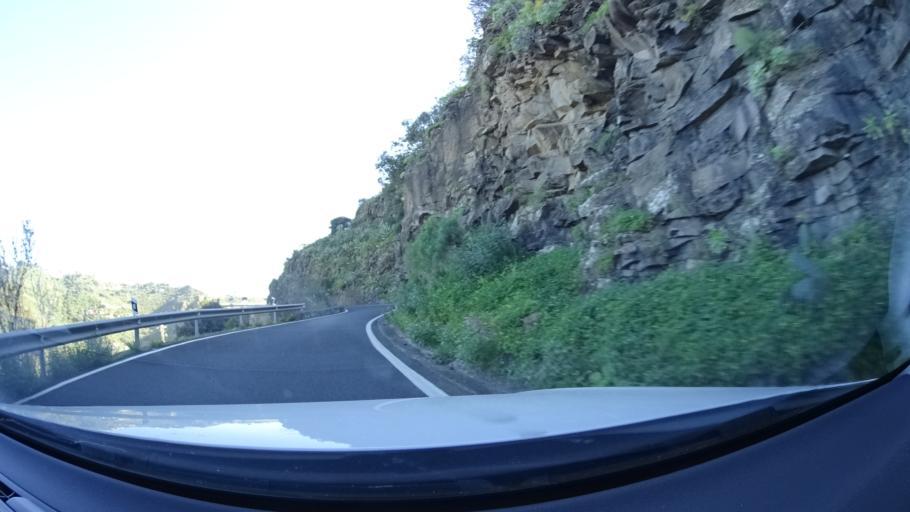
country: ES
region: Canary Islands
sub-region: Provincia de Las Palmas
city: Santa Brigida
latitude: 28.0195
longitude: -15.4705
